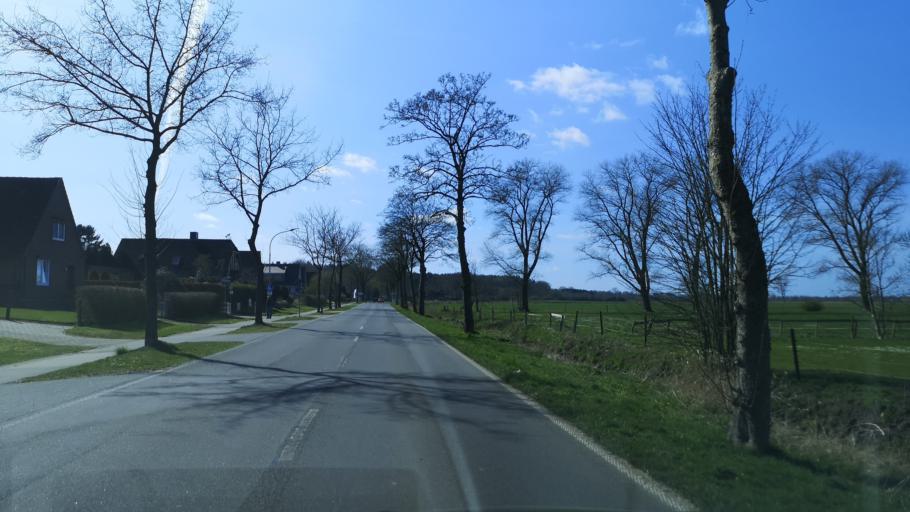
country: DE
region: Schleswig-Holstein
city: Munsterdorf
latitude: 53.9052
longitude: 9.5381
